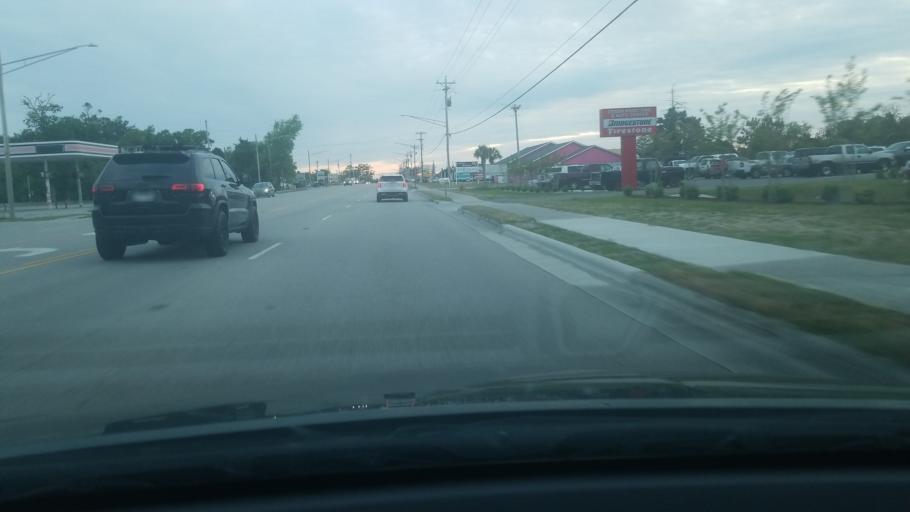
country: US
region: North Carolina
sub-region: Carteret County
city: Cedar Point
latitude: 34.6846
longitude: -77.0801
